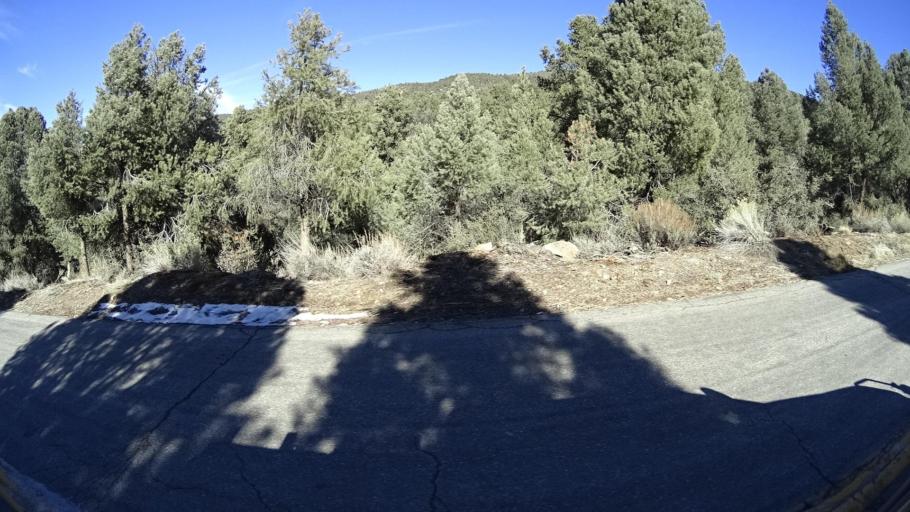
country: US
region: California
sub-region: Kern County
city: Pine Mountain Club
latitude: 34.8612
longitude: -119.2193
